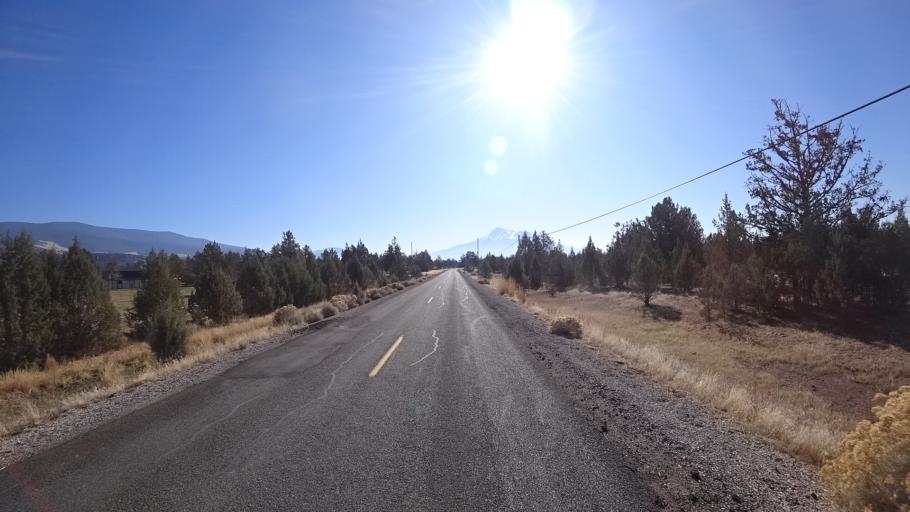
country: US
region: California
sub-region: Siskiyou County
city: Montague
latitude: 41.6542
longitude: -122.3623
